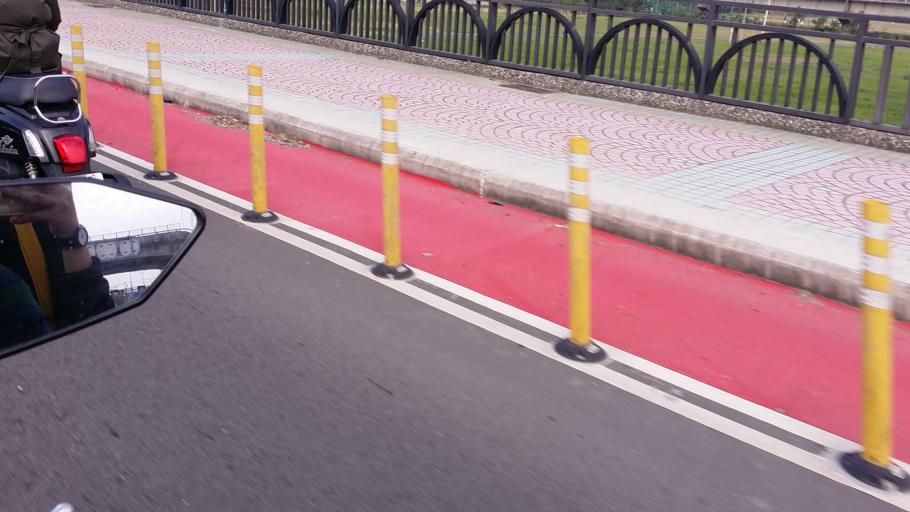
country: TW
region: Taiwan
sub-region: Hsinchu
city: Zhubei
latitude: 24.8201
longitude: 120.9960
